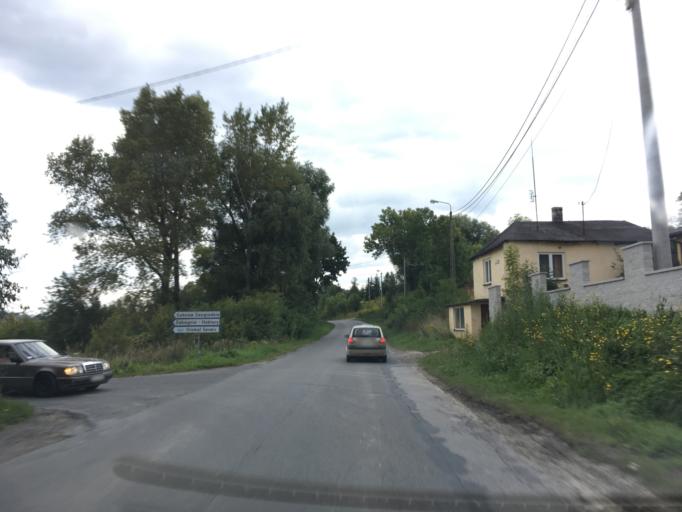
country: PL
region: Lesser Poland Voivodeship
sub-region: Powiat olkuski
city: Wolbrom
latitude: 50.3936
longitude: 19.7636
